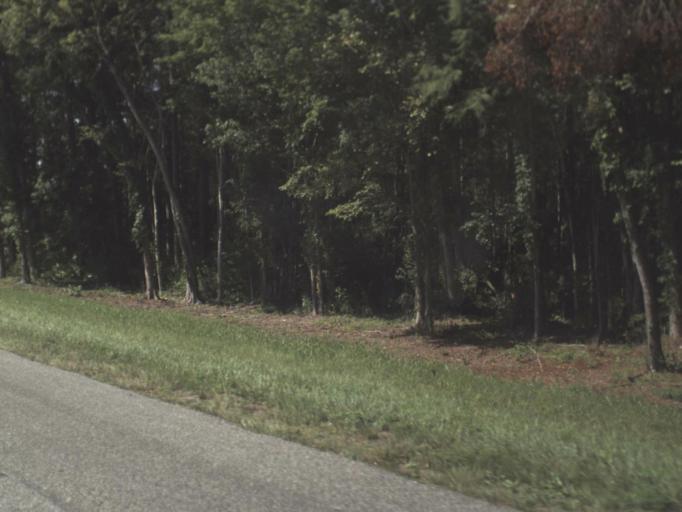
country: US
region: Florida
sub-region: Saint Johns County
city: Fruit Cove
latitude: 30.0210
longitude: -81.4831
